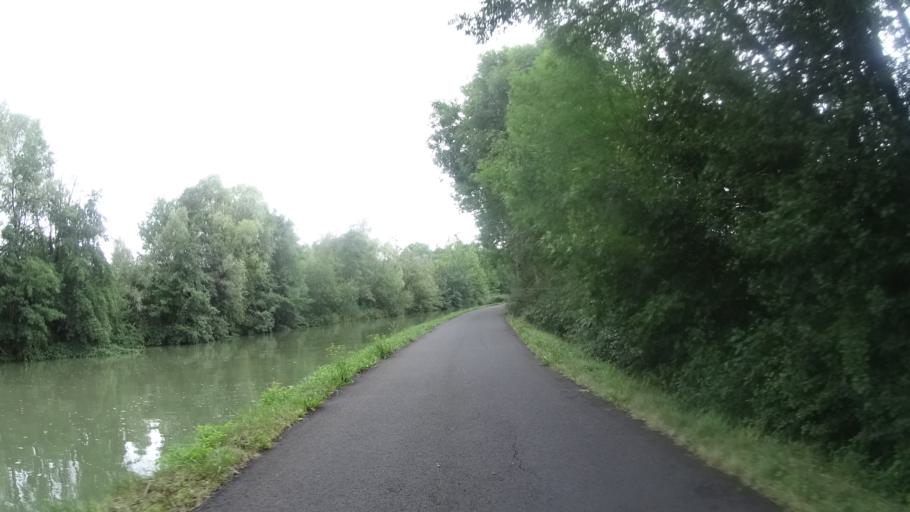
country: FR
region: Lorraine
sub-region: Departement de Meurthe-et-Moselle
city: Einville-au-Jard
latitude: 48.6697
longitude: 6.5185
